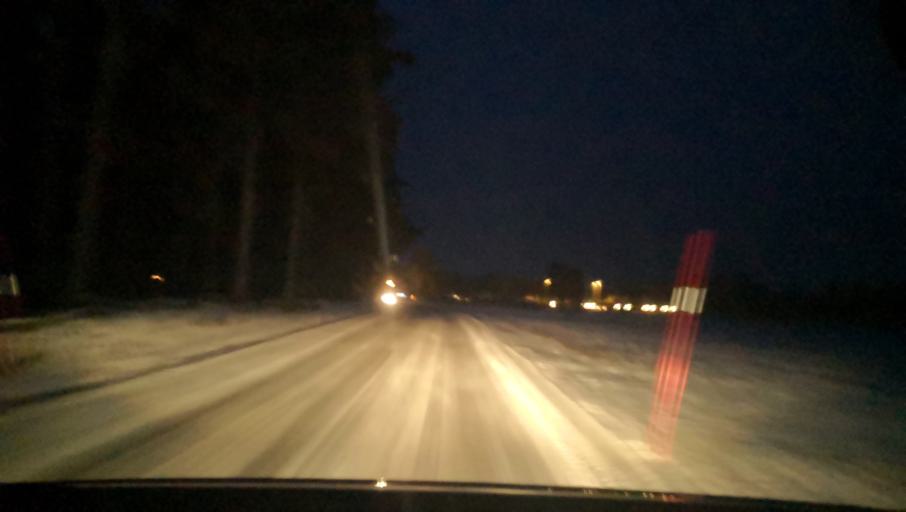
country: SE
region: Uppsala
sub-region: Heby Kommun
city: Tarnsjo
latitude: 60.2964
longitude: 16.8051
